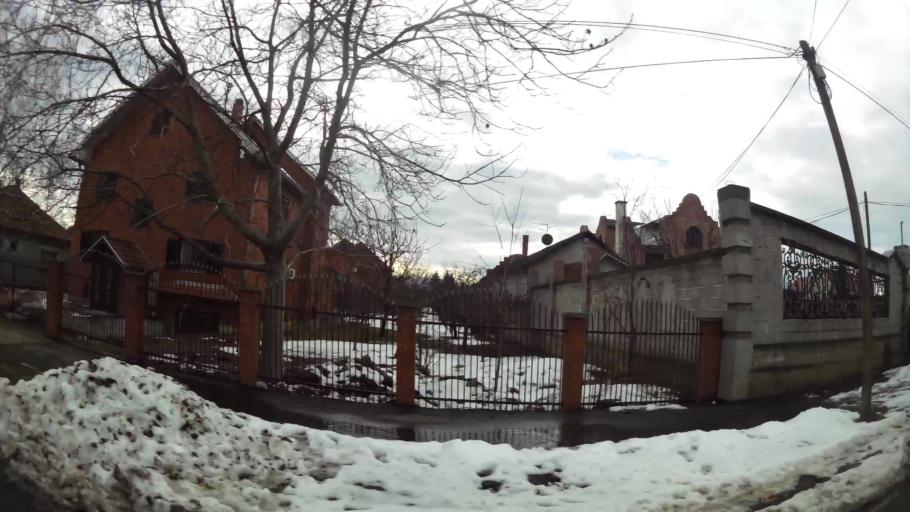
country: RS
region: Central Serbia
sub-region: Belgrade
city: Surcin
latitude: 44.8002
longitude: 20.2892
